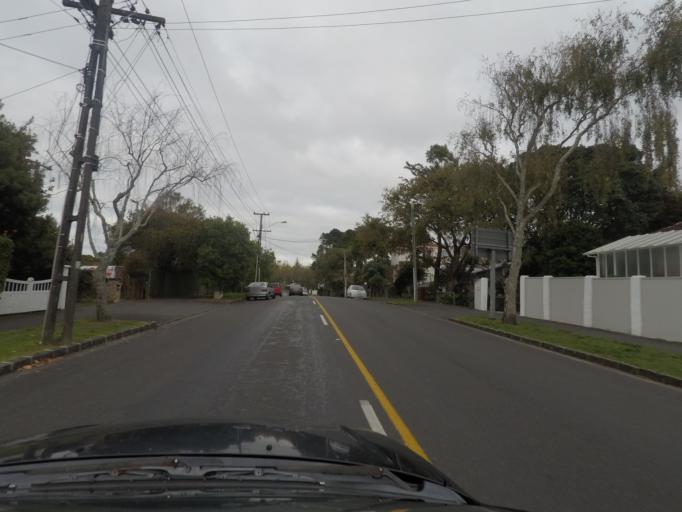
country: NZ
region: Auckland
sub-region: Auckland
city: Auckland
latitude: -36.8888
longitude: 174.7688
